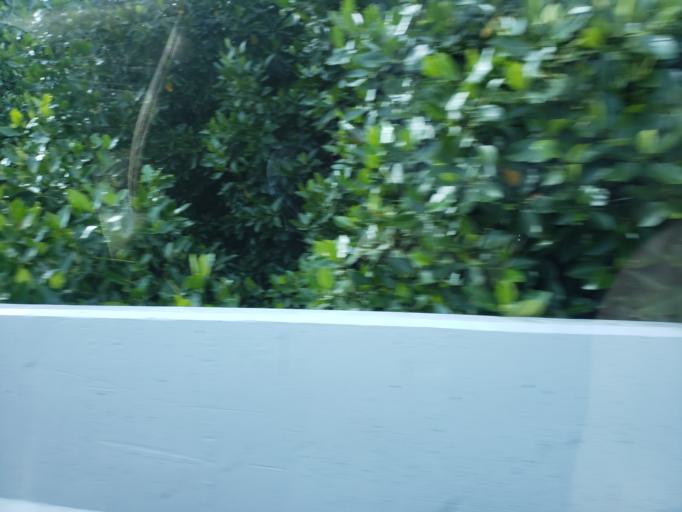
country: ID
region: Bali
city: Kelanabian
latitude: -8.7453
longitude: 115.1835
